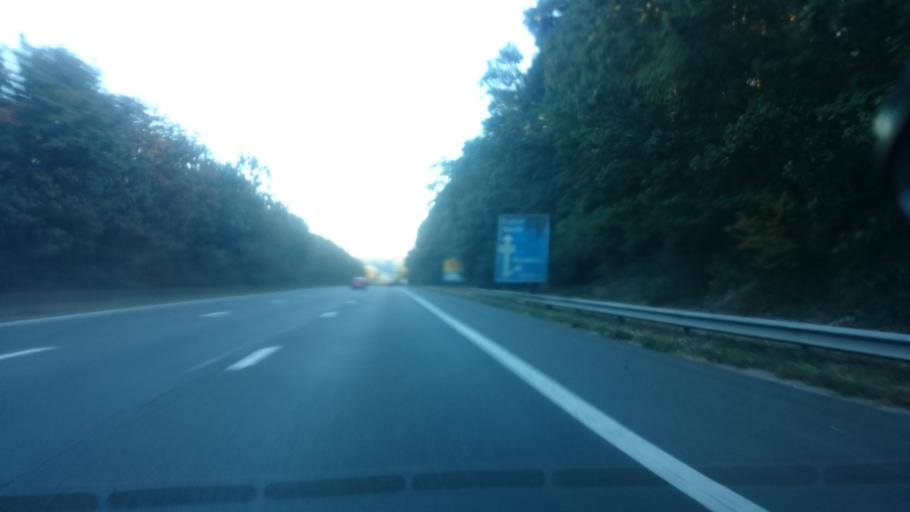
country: BE
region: Flanders
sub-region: Provincie Vlaams-Brabant
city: Overijse
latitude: 50.7429
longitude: 4.5448
